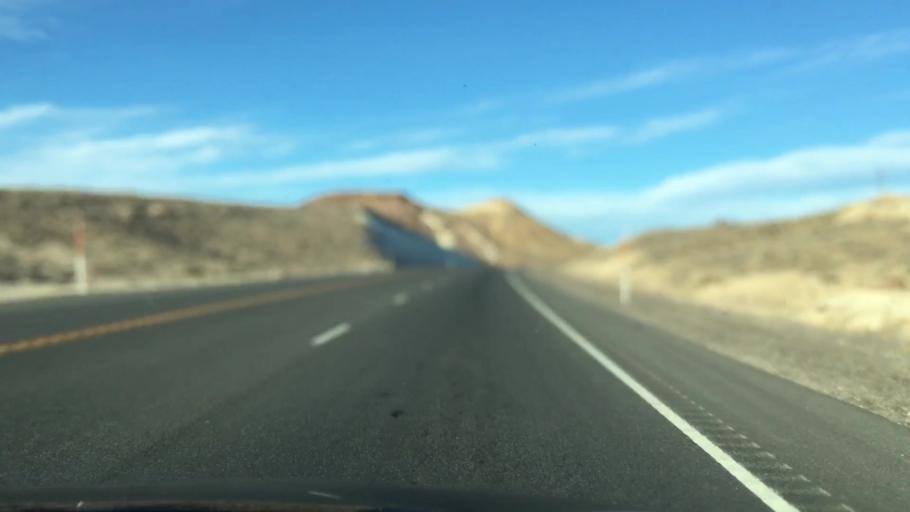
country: US
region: Nevada
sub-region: Nye County
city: Tonopah
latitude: 37.9927
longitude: -117.2726
